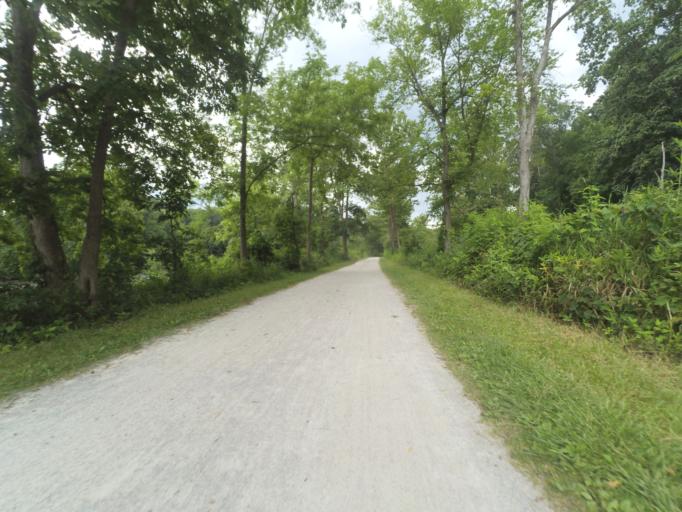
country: US
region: Ohio
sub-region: Summit County
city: Peninsula
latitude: 41.2551
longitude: -81.5502
